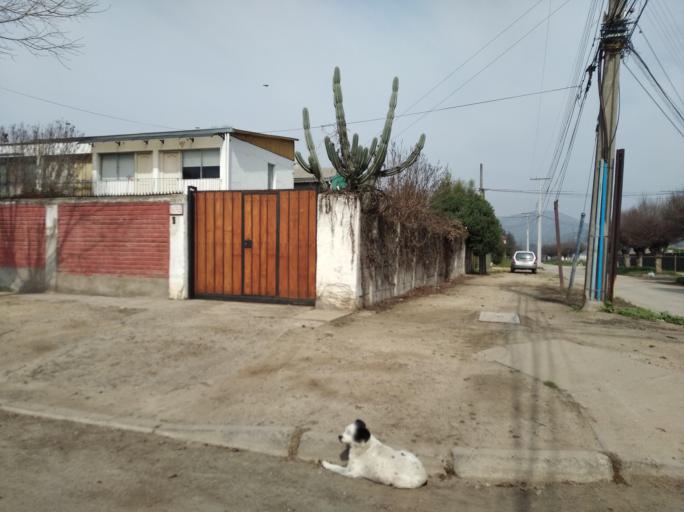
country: CL
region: Valparaiso
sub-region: Provincia de Marga Marga
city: Limache
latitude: -32.9881
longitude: -71.2791
